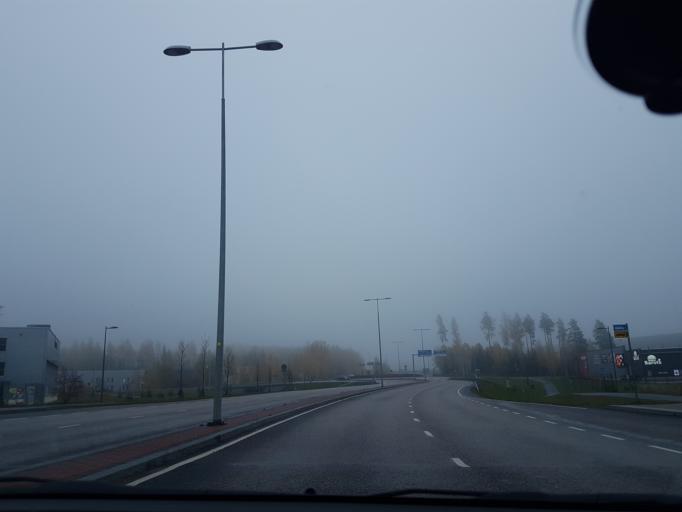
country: FI
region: Uusimaa
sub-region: Helsinki
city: Jaervenpaeae
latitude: 60.4563
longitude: 25.1139
